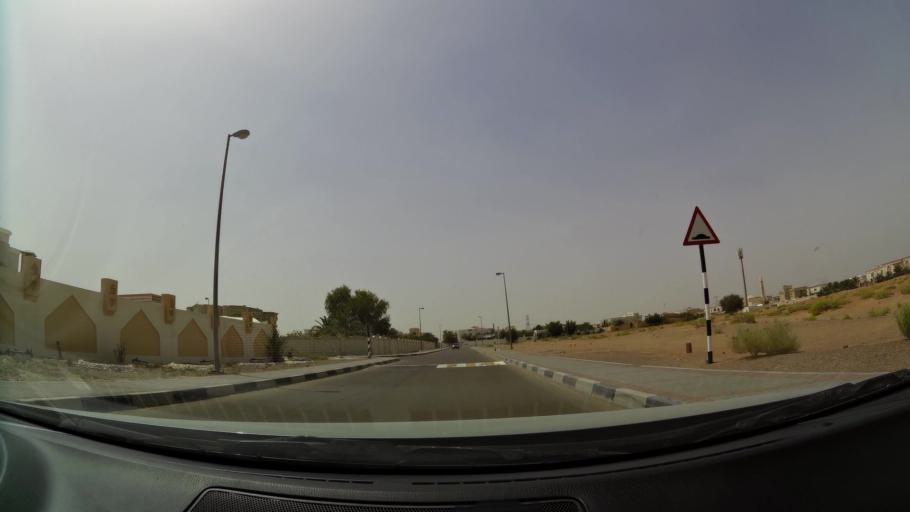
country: AE
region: Abu Dhabi
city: Al Ain
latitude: 24.1485
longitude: 55.6476
